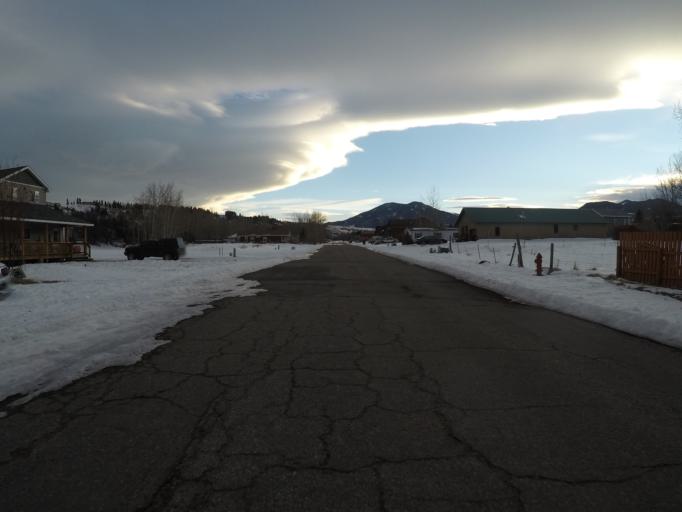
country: US
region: Montana
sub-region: Carbon County
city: Red Lodge
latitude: 45.1950
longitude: -109.2433
